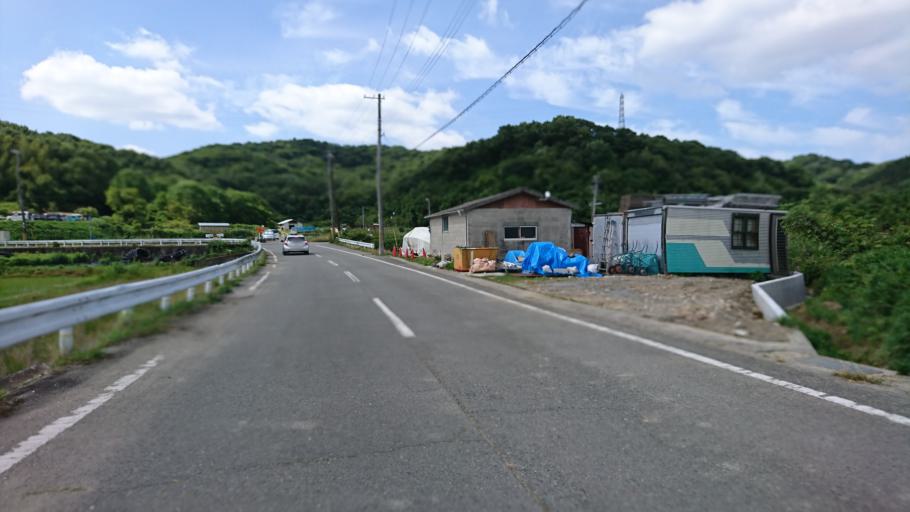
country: JP
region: Hyogo
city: Shirahamacho-usazakiminami
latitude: 34.7929
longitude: 134.7409
